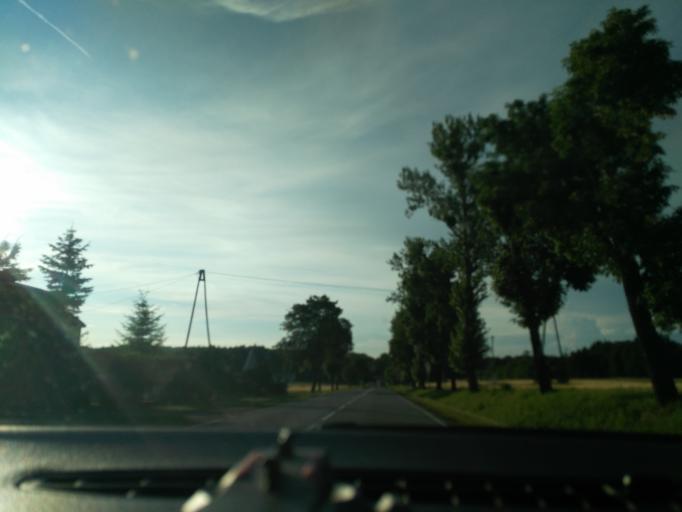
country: PL
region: Lublin Voivodeship
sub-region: Powiat krasnicki
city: Szastarka
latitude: 50.8420
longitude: 22.2972
